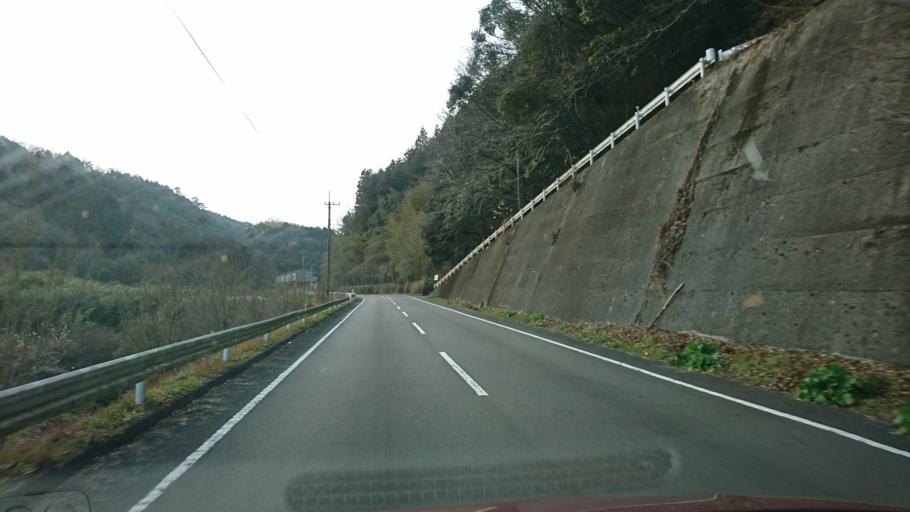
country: JP
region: Ehime
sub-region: Shikoku-chuo Shi
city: Matsuyama
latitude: 33.8994
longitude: 132.8304
